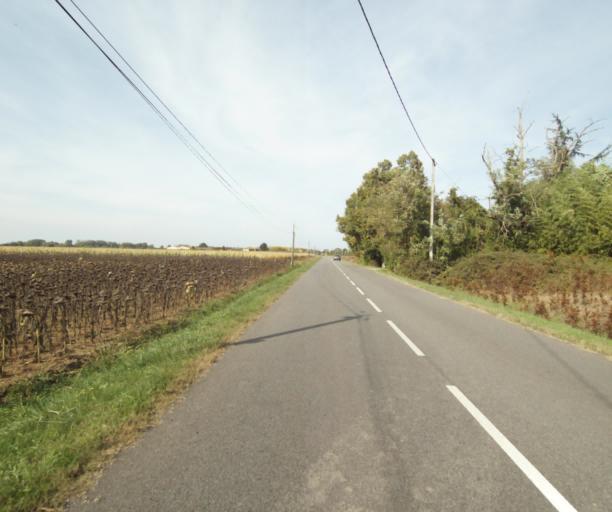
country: FR
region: Midi-Pyrenees
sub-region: Departement du Tarn-et-Garonne
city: Corbarieu
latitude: 43.9323
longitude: 1.3815
